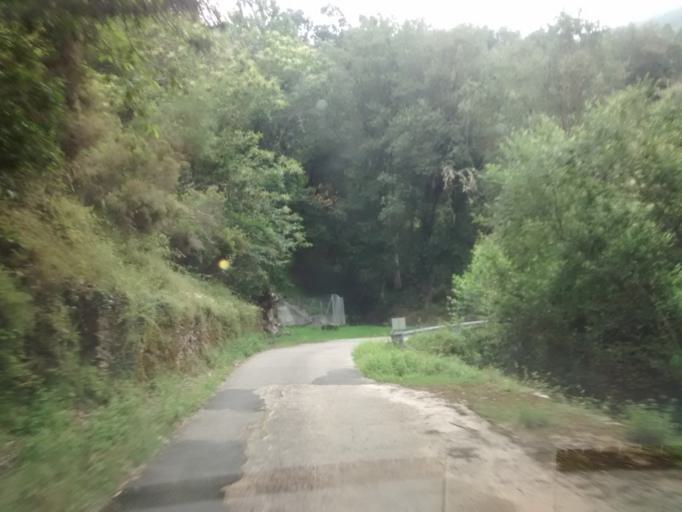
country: ES
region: Galicia
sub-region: Provincia de Ourense
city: Castro Caldelas
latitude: 42.4246
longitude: -7.3868
